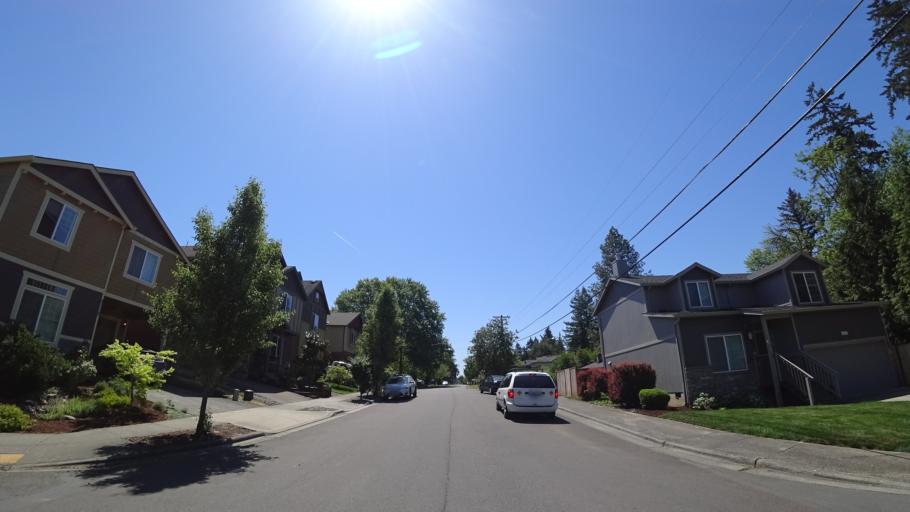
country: US
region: Oregon
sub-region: Washington County
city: Aloha
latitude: 45.4973
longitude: -122.8566
